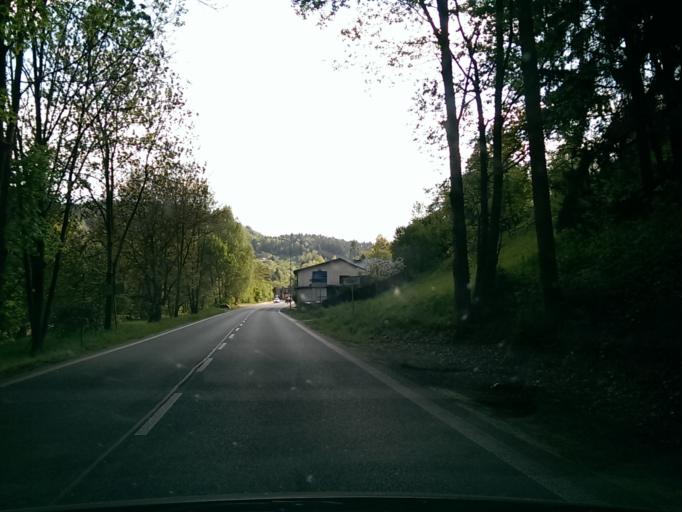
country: CZ
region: Liberecky
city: Mala Skala
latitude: 50.6510
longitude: 15.2115
